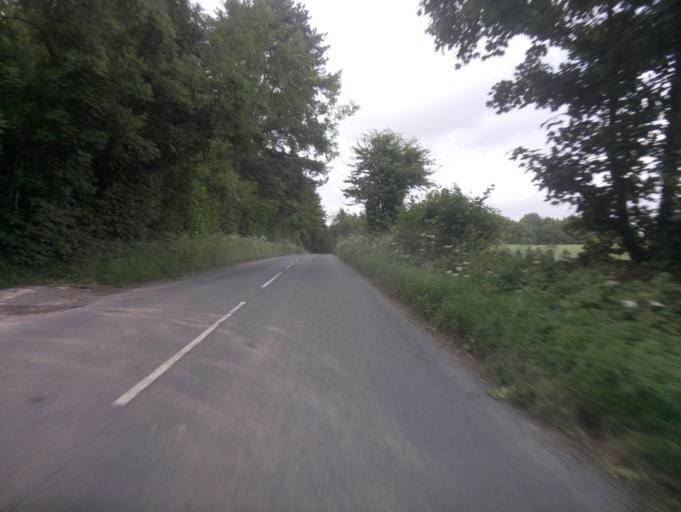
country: GB
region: England
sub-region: Gloucestershire
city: Moreton in Marsh
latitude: 51.9959
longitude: -1.7567
